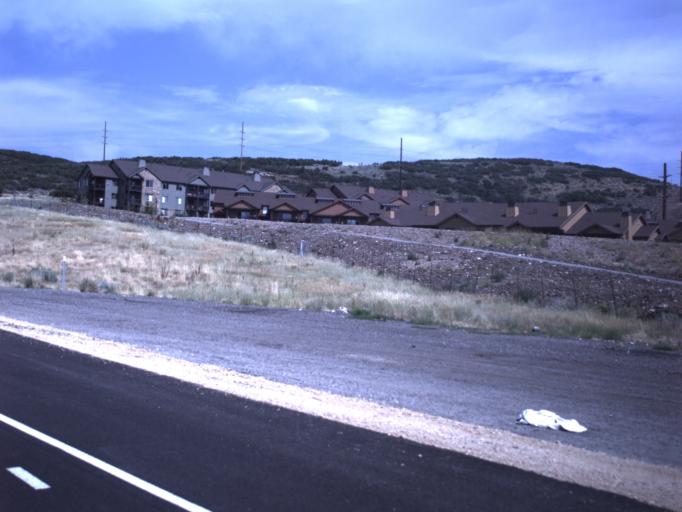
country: US
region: Utah
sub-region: Summit County
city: Park City
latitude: 40.6799
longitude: -111.4346
